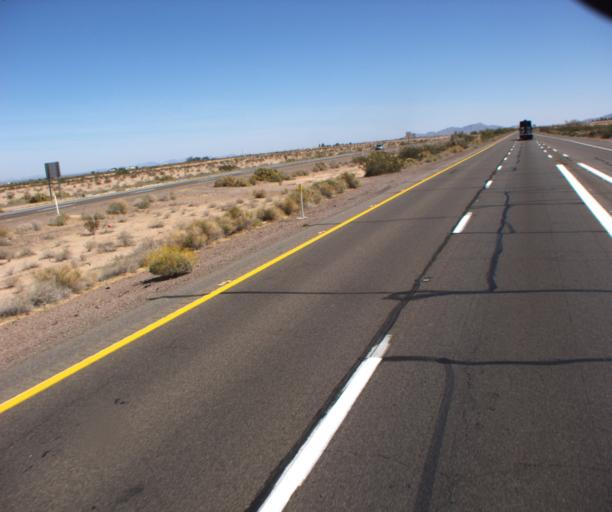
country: US
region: Arizona
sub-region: Yuma County
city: Wellton
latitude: 32.6822
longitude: -114.0184
